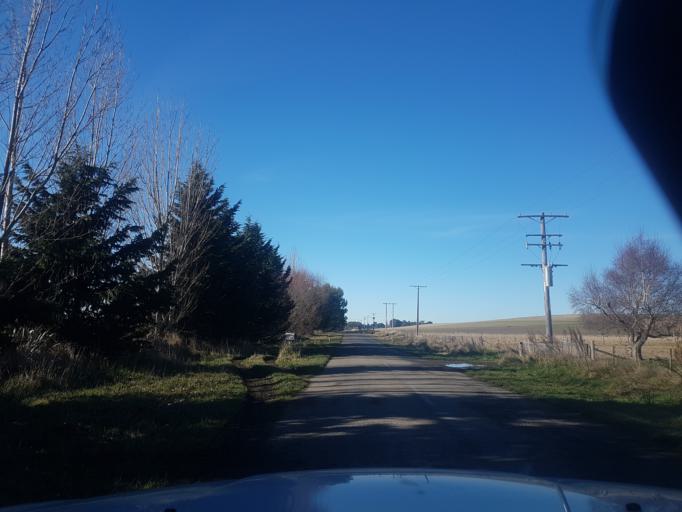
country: NZ
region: Canterbury
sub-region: Timaru District
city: Pleasant Point
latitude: -44.2904
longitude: 171.0663
